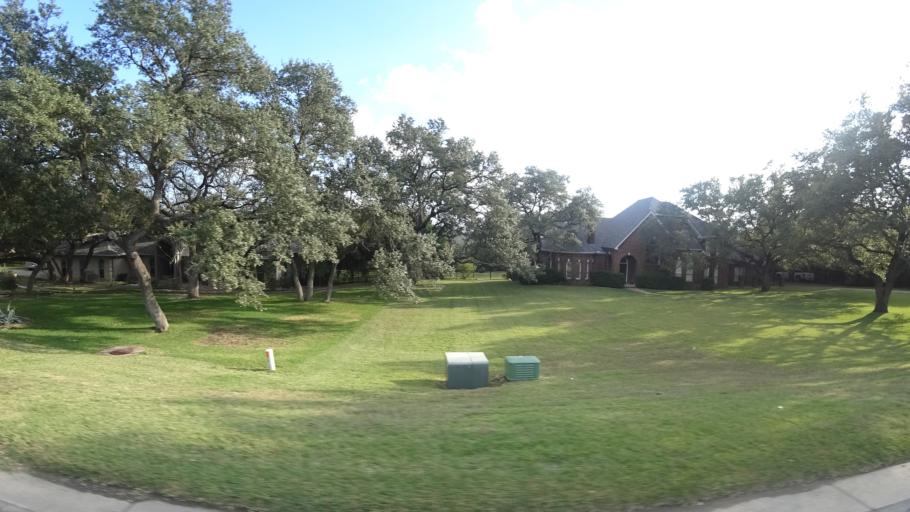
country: US
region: Texas
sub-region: Travis County
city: Barton Creek
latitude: 30.2816
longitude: -97.8787
